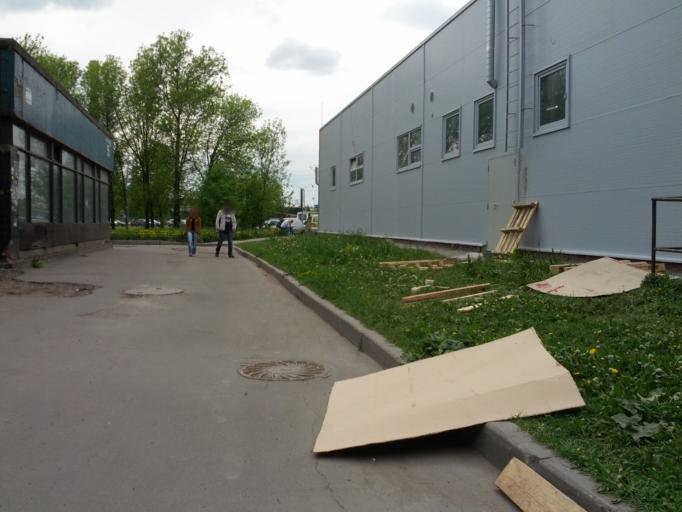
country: RU
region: St.-Petersburg
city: Obukhovo
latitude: 59.8939
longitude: 30.4645
